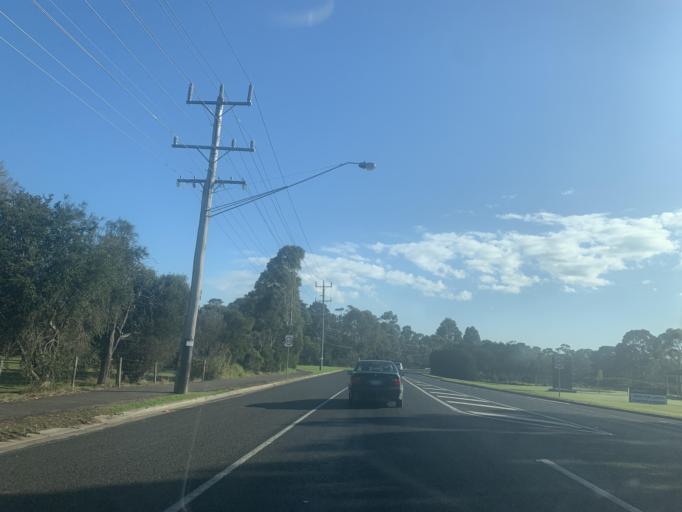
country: AU
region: Victoria
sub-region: Mornington Peninsula
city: Hastings
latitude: -38.2992
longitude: 145.1906
